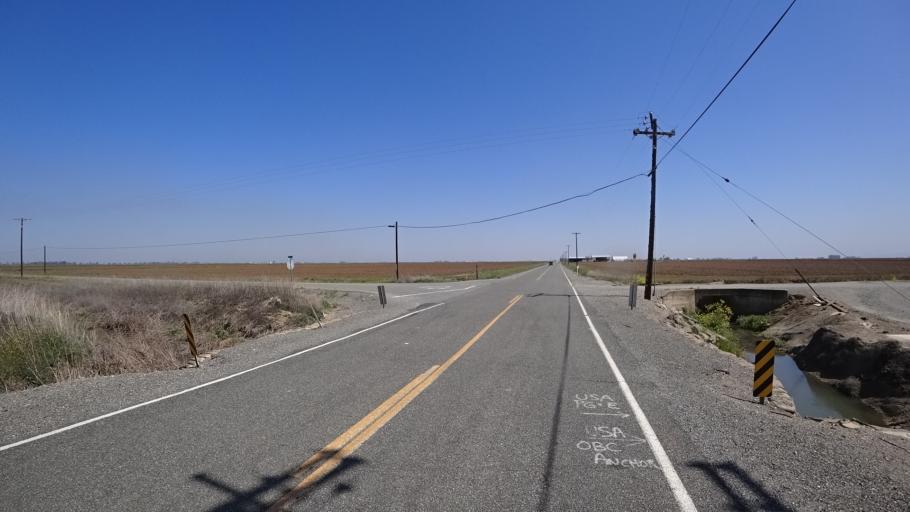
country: US
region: California
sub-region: Glenn County
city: Willows
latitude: 39.4948
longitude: -122.1748
